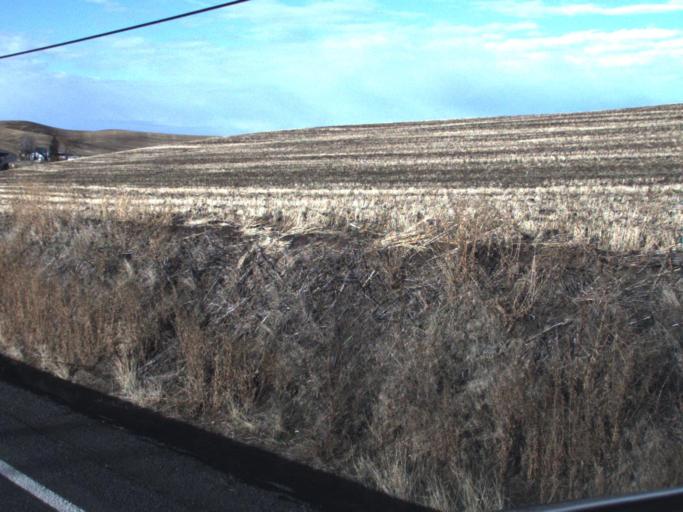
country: US
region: Washington
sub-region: Whitman County
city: Pullman
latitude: 46.7250
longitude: -117.2303
